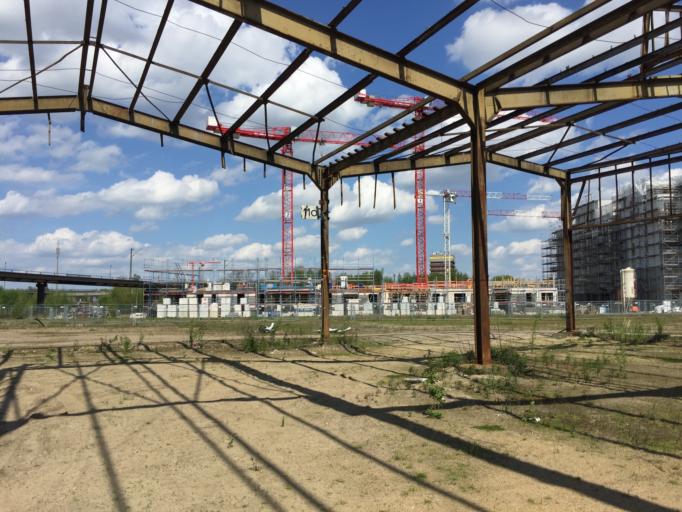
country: DE
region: Hamburg
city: Altona
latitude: 53.5605
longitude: 9.9368
